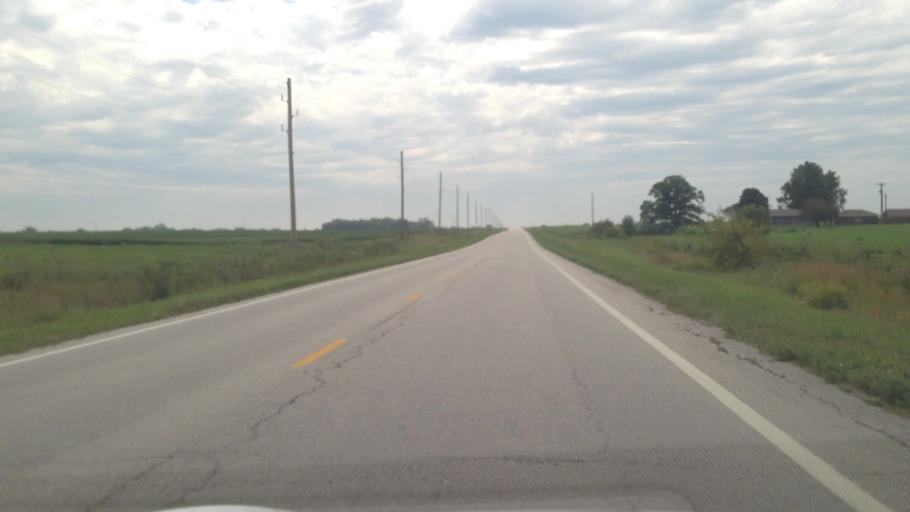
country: US
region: Kansas
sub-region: Allen County
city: Iola
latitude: 37.9422
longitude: -95.1701
